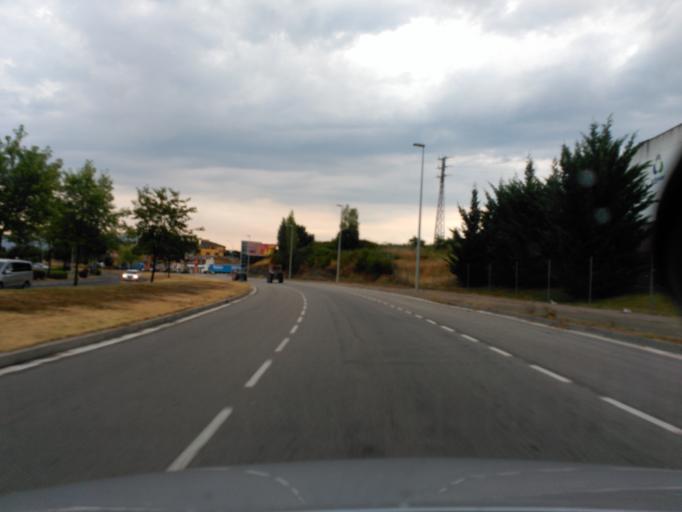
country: ES
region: Catalonia
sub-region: Provincia de Barcelona
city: Vic
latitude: 41.9462
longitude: 2.2681
